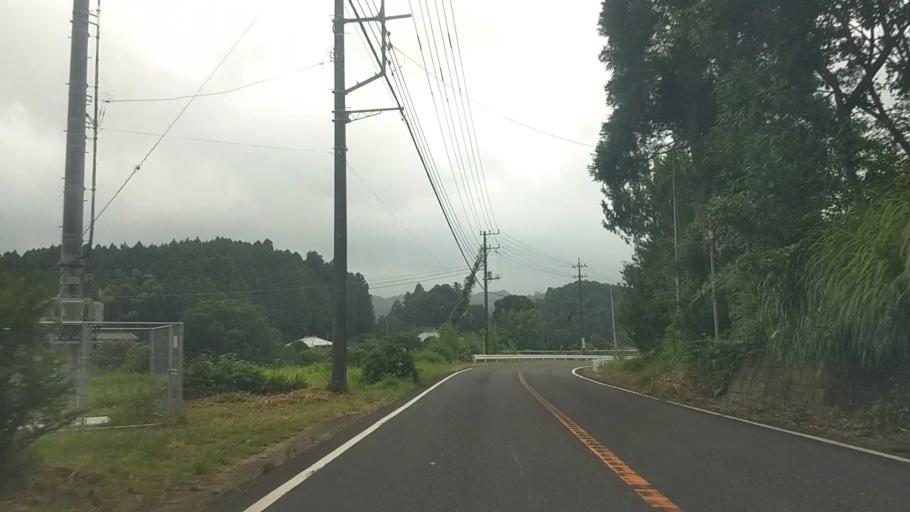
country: JP
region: Chiba
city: Kawaguchi
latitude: 35.2306
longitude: 140.0750
